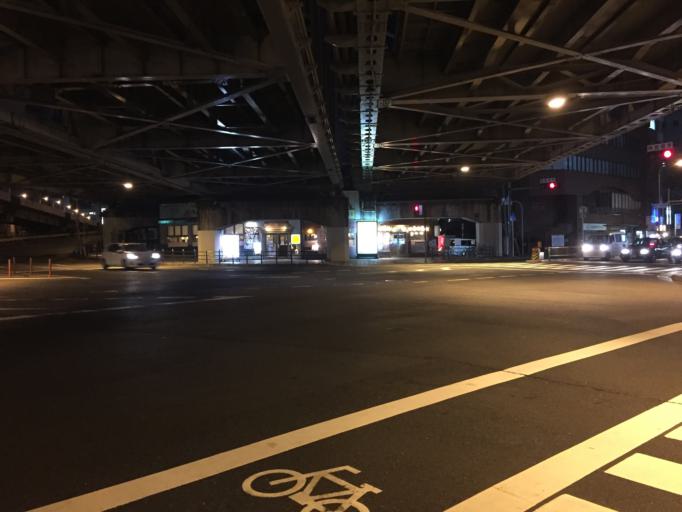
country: JP
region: Osaka
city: Osaka-shi
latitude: 34.7090
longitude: 135.4964
